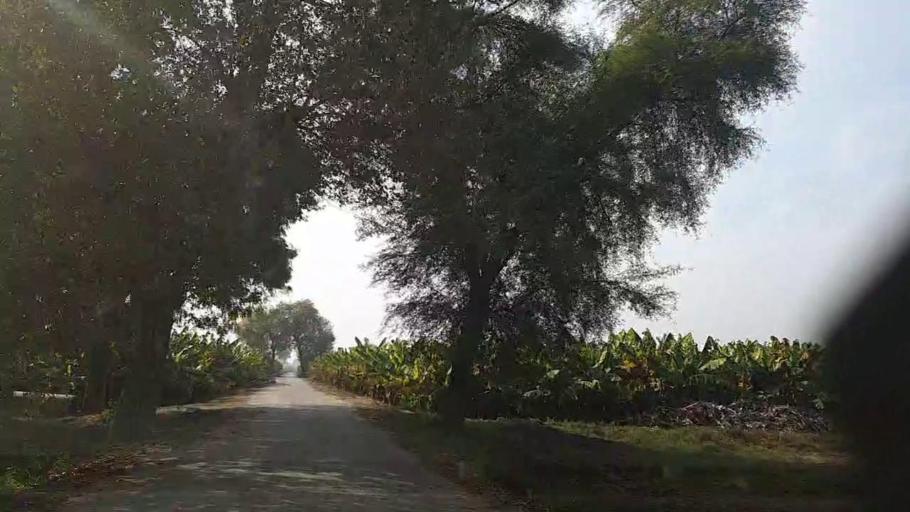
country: PK
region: Sindh
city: Daur
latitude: 26.3994
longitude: 68.2108
